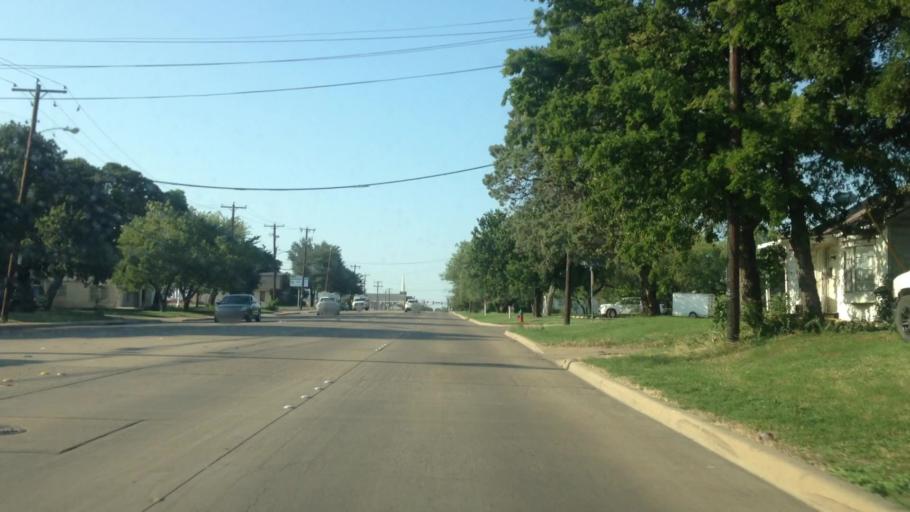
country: US
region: Texas
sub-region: Tarrant County
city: Haltom City
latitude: 32.8013
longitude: -97.2557
